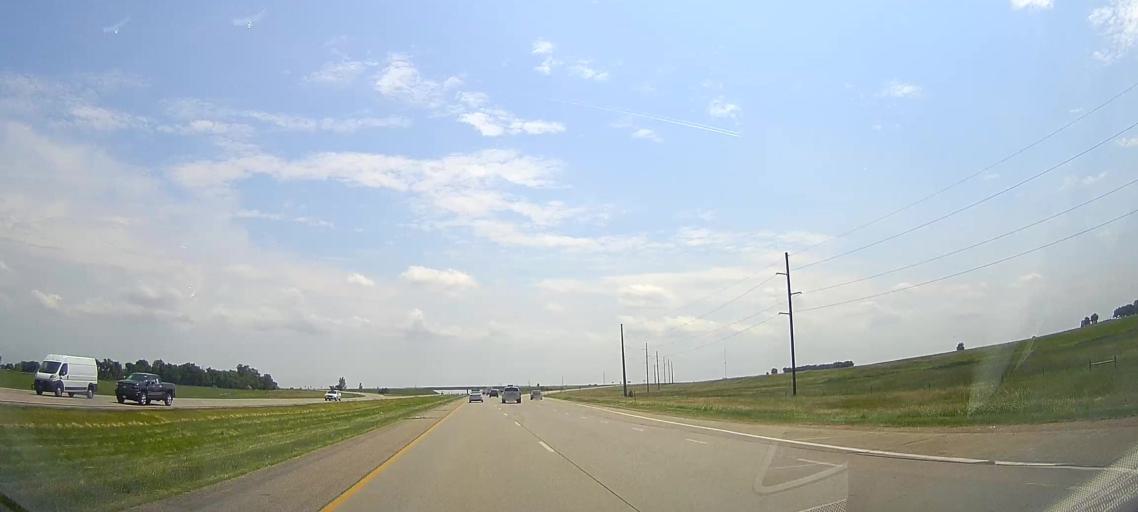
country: US
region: South Dakota
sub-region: Lincoln County
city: Tea
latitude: 43.3938
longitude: -96.7965
